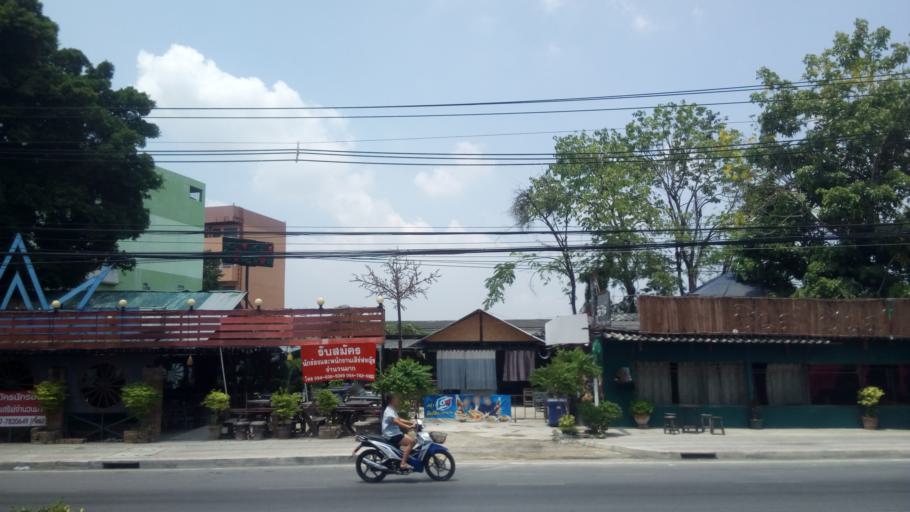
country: TH
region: Pathum Thani
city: Pathum Thani
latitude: 14.0264
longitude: 100.5254
